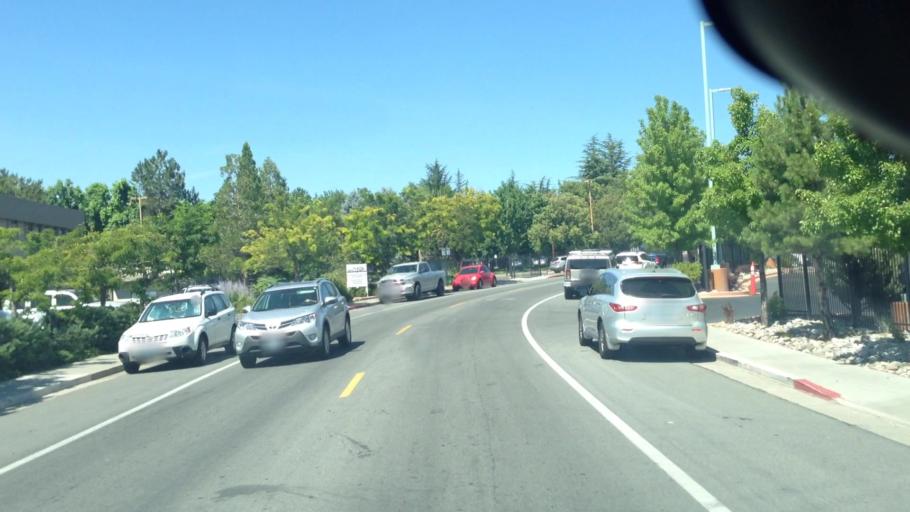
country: US
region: Nevada
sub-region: Washoe County
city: Reno
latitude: 39.4953
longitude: -119.8011
